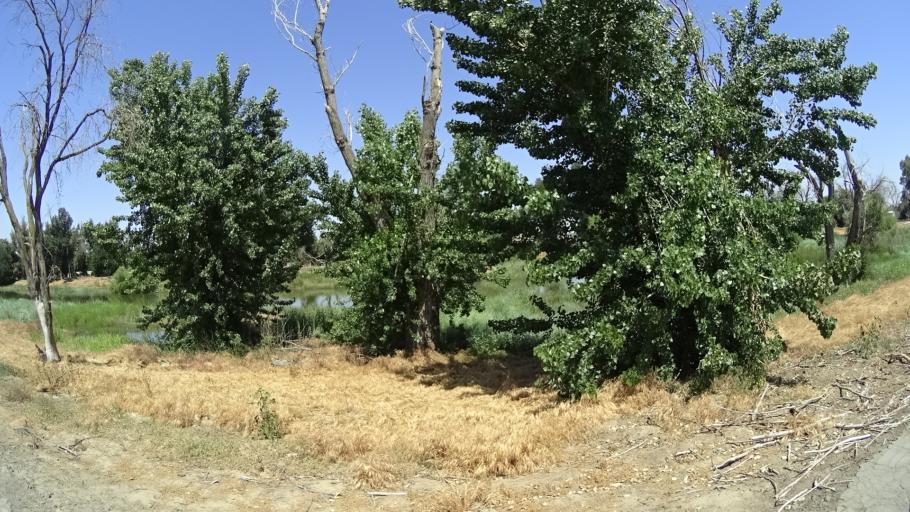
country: US
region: California
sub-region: Kings County
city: Lemoore
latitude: 36.3637
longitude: -119.8079
